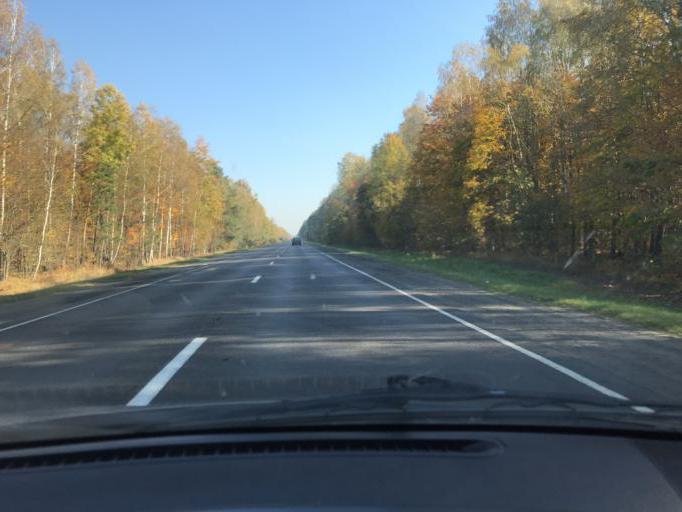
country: BY
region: Brest
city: Mikashevichy
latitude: 52.2436
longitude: 27.3446
